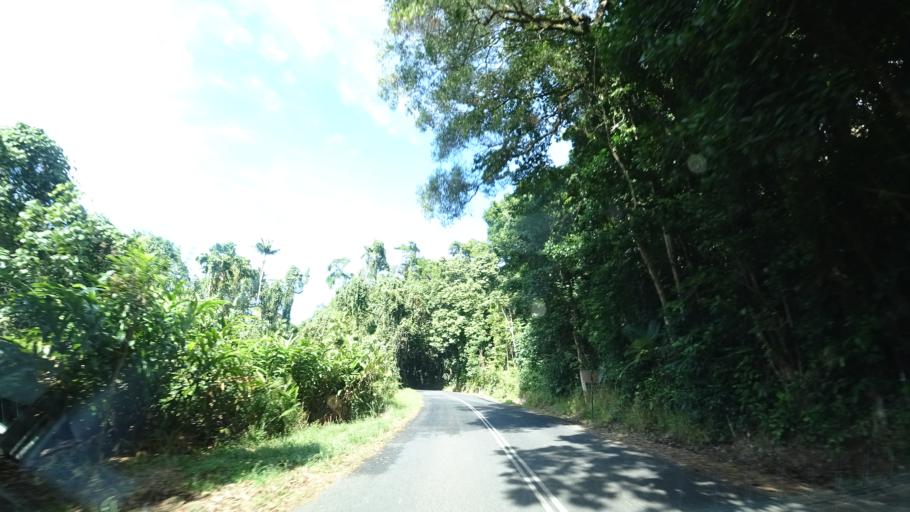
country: AU
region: Queensland
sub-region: Cairns
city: Port Douglas
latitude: -16.1107
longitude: 145.4568
